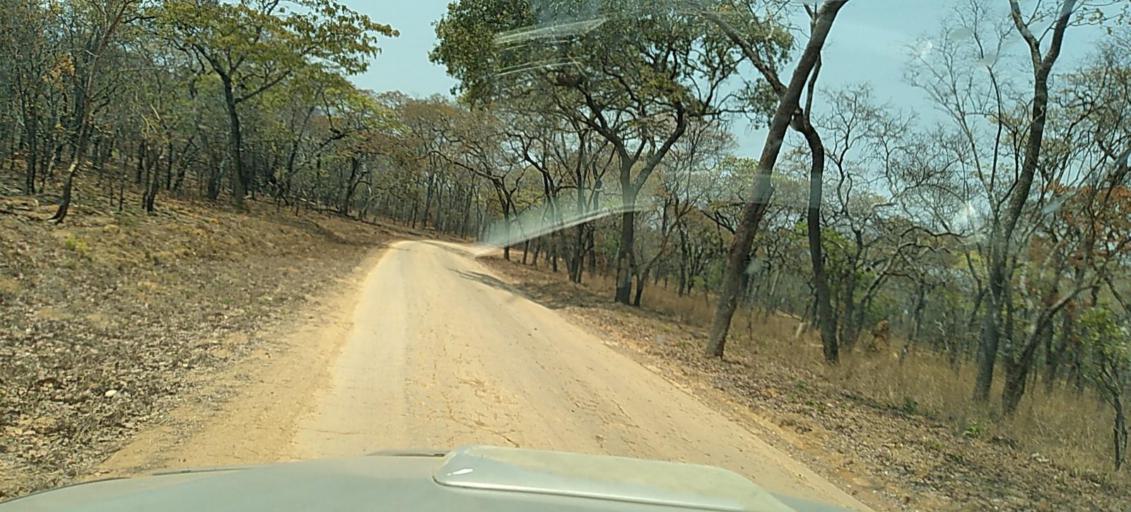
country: ZM
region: North-Western
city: Kasempa
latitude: -13.6073
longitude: 26.1753
